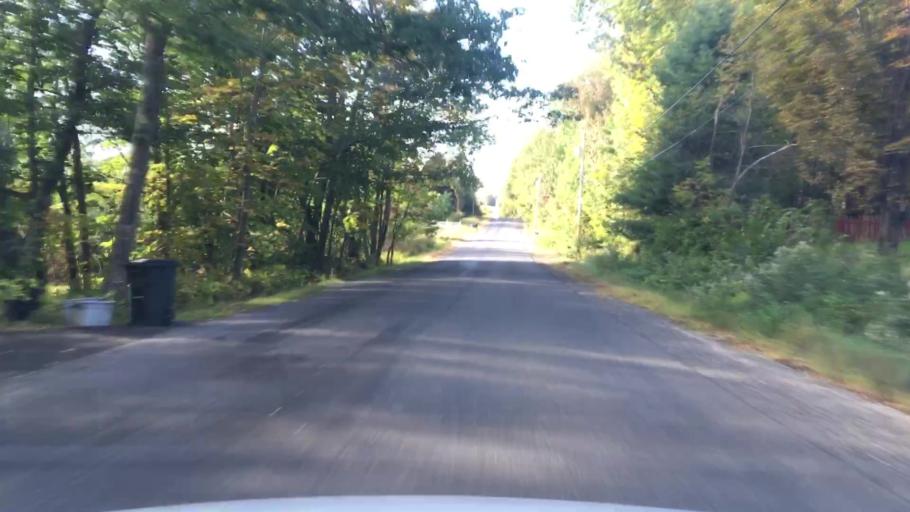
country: US
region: Maine
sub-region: Androscoggin County
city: Lisbon Falls
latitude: 43.9612
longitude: -70.0562
